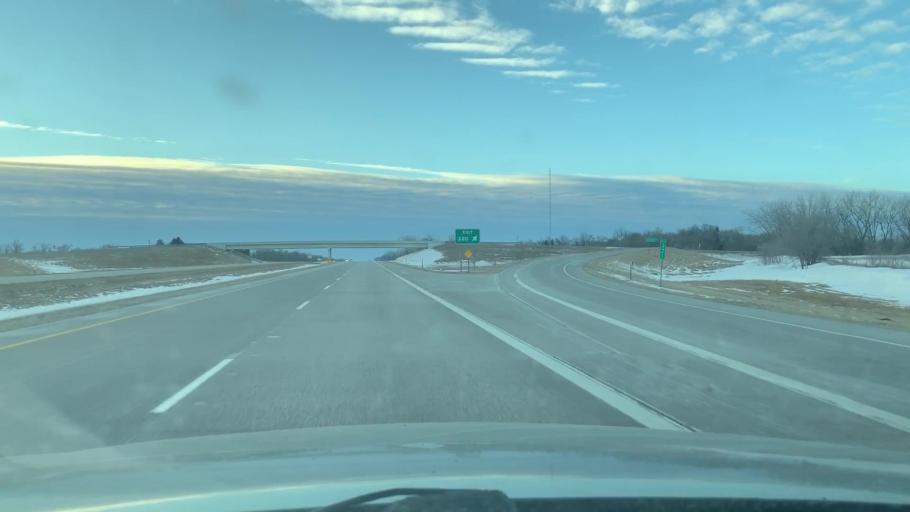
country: US
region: North Dakota
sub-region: Cass County
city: Casselton
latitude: 46.8763
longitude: -97.4253
